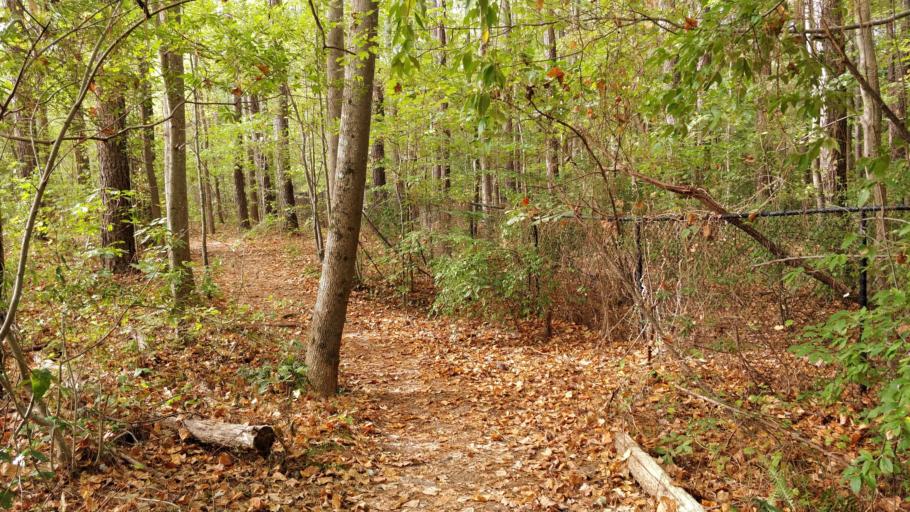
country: US
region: North Carolina
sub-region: Wake County
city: West Raleigh
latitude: 35.9067
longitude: -78.6709
